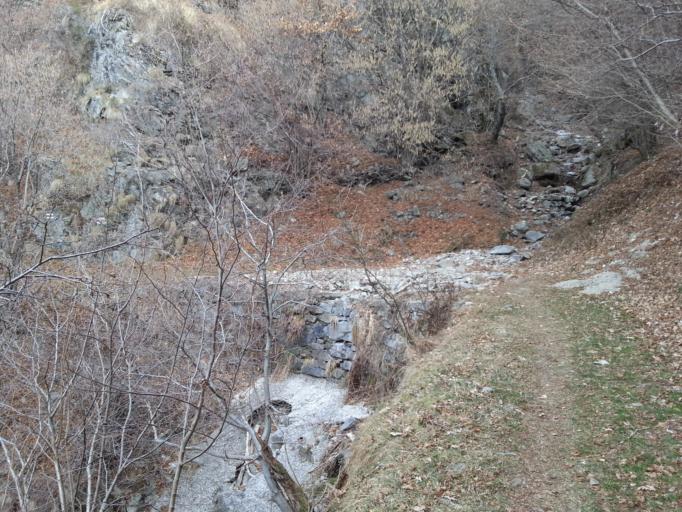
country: CH
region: Ticino
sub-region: Lugano District
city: Gravesano
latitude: 46.0619
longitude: 8.8839
